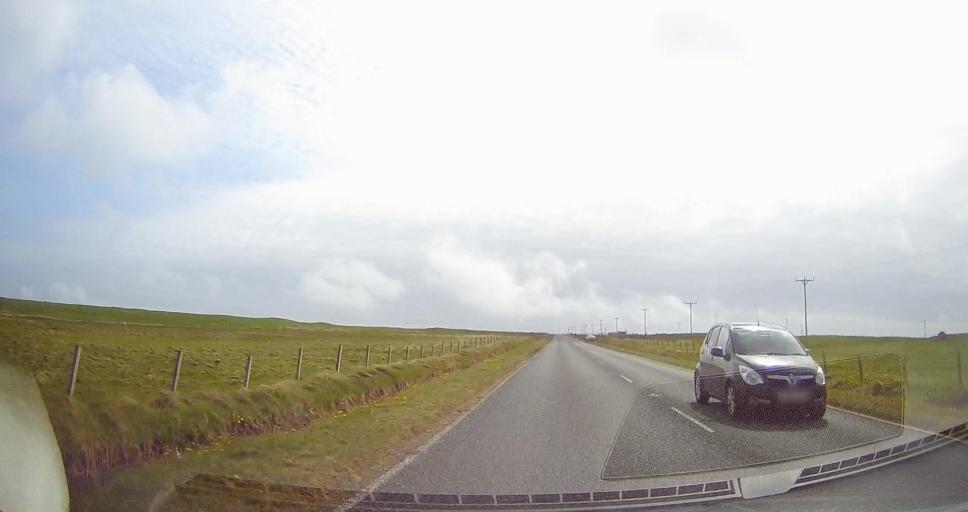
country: GB
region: Scotland
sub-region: Shetland Islands
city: Sandwick
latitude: 59.9033
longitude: -1.3028
